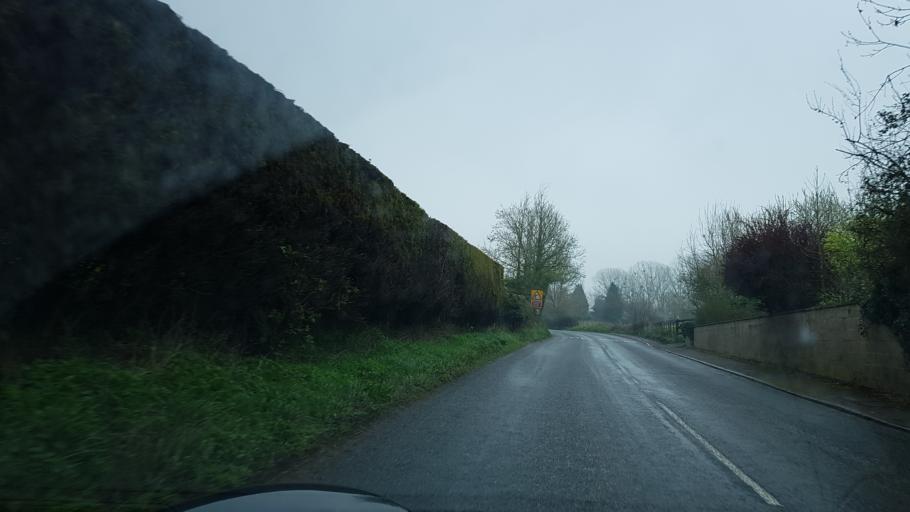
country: GB
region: England
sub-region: Herefordshire
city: Donnington
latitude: 51.9774
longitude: -2.4337
